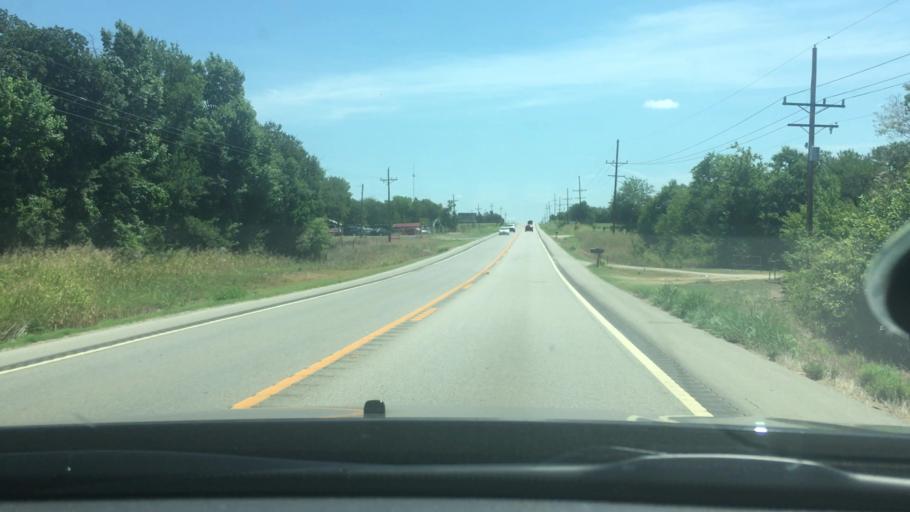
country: US
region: Oklahoma
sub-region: Bryan County
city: Durant
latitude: 33.9975
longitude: -96.2842
